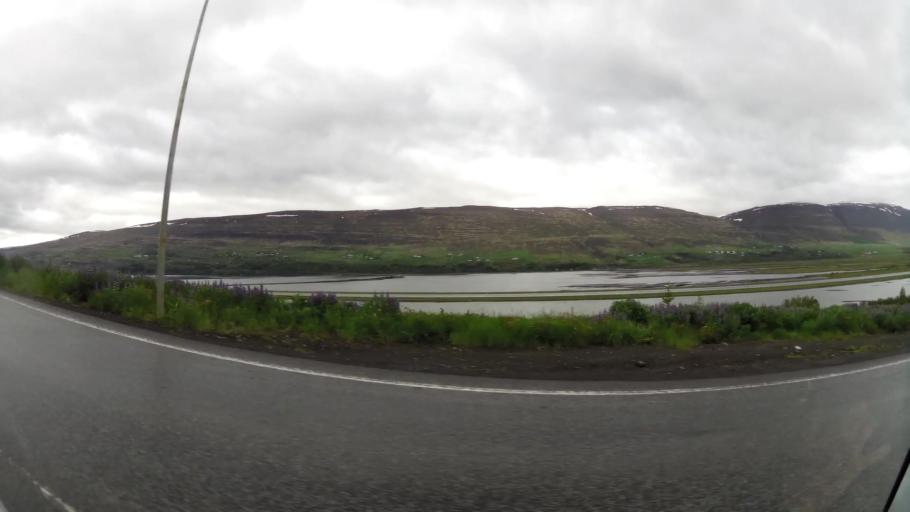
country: IS
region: Northeast
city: Akureyri
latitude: 65.6629
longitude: -18.0859
